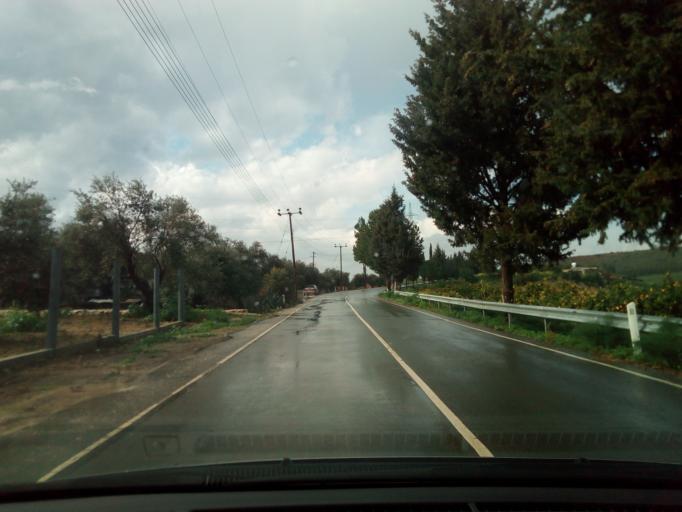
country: CY
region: Pafos
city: Polis
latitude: 35.0204
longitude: 32.4461
